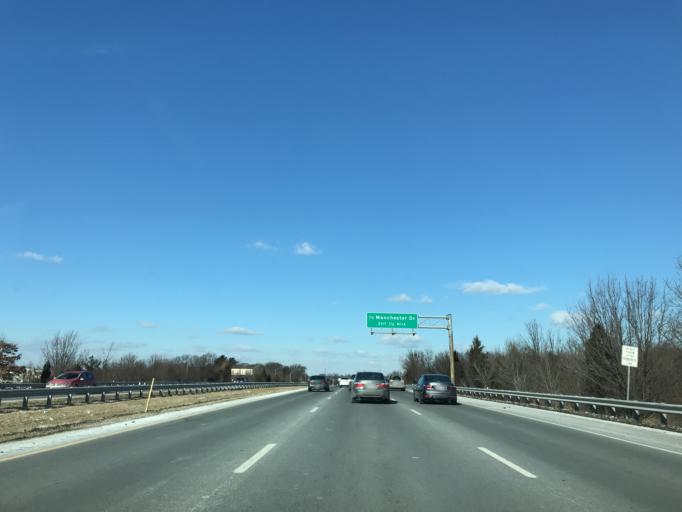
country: US
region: Maryland
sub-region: Prince George's County
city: Camp Springs
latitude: 38.8056
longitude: -76.9062
